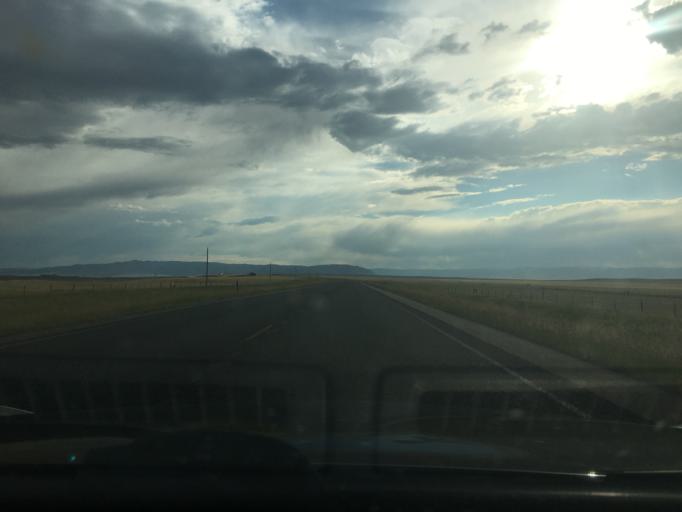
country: US
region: Wyoming
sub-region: Albany County
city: Laramie
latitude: 41.3209
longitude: -105.7562
